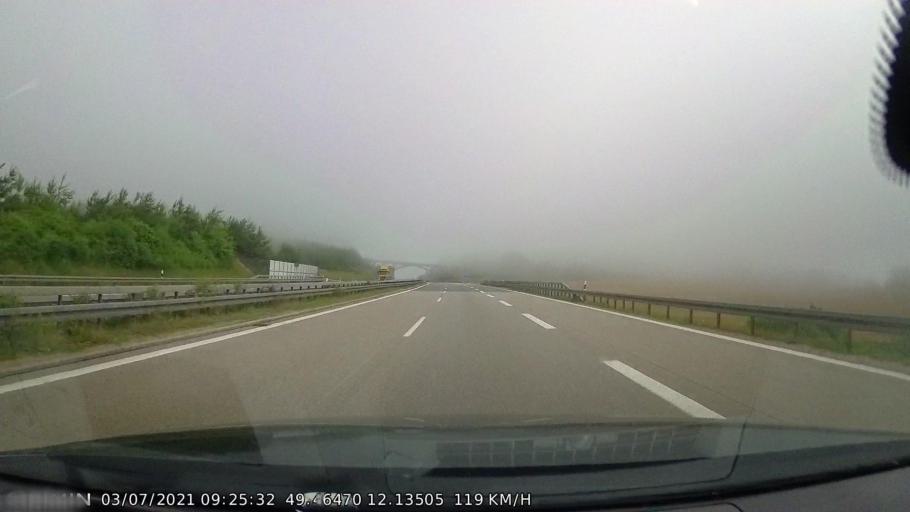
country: DE
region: Bavaria
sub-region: Upper Palatinate
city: Nabburg
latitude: 49.4648
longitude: 12.1351
